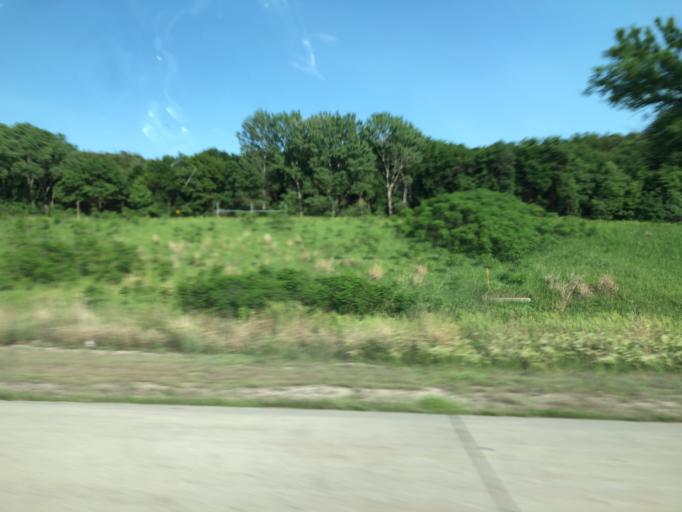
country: US
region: Nebraska
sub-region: Saunders County
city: Ashland
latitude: 41.0626
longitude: -96.2928
